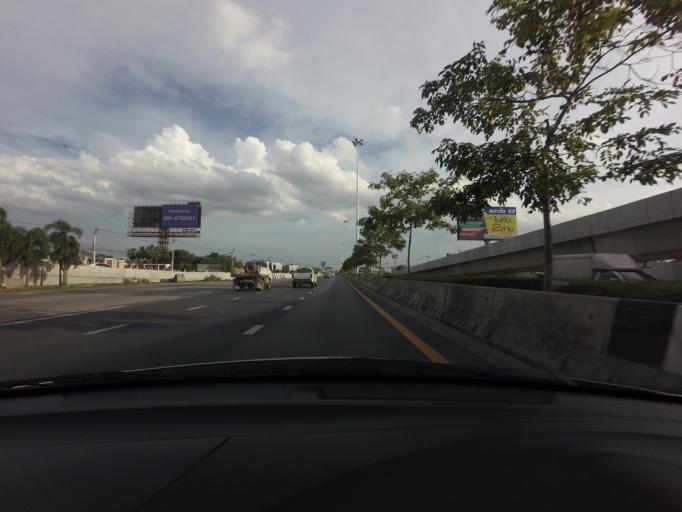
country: TH
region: Nonthaburi
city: Bang Bua Thong
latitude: 13.9256
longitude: 100.4530
